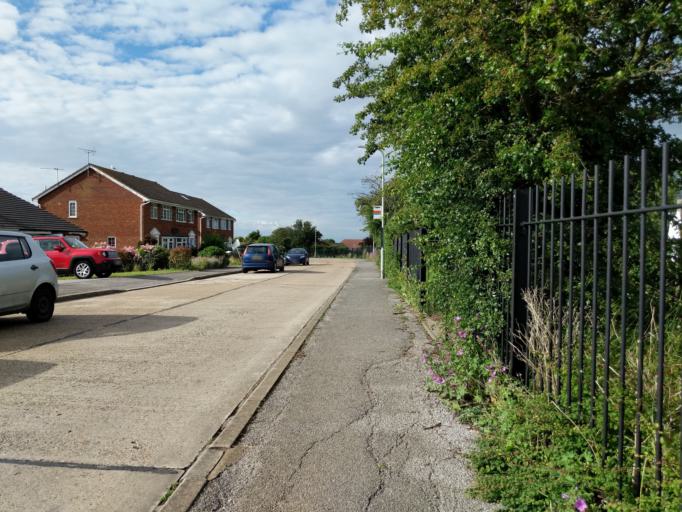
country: GB
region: England
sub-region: Kent
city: Whitstable
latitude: 51.3461
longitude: 1.0107
